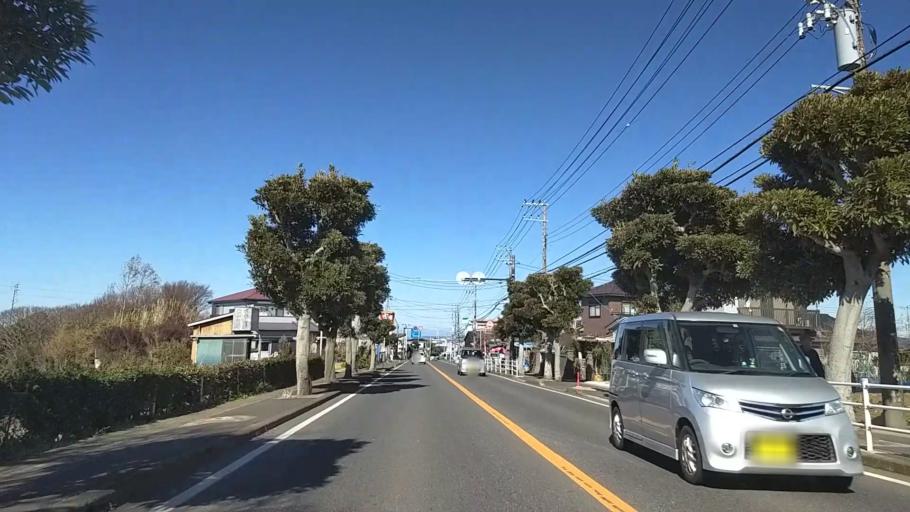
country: JP
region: Kanagawa
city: Miura
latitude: 35.1730
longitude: 139.6360
